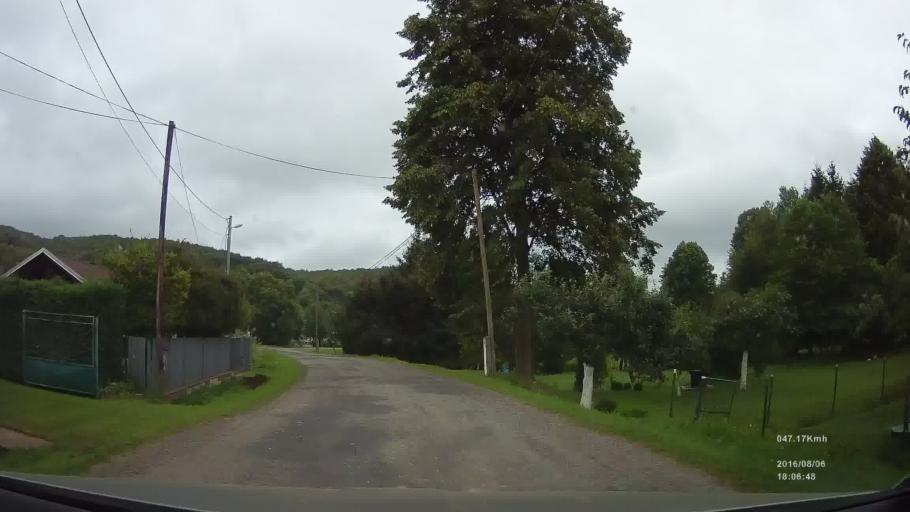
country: SK
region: Presovsky
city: Svidnik
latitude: 49.4009
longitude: 21.5701
